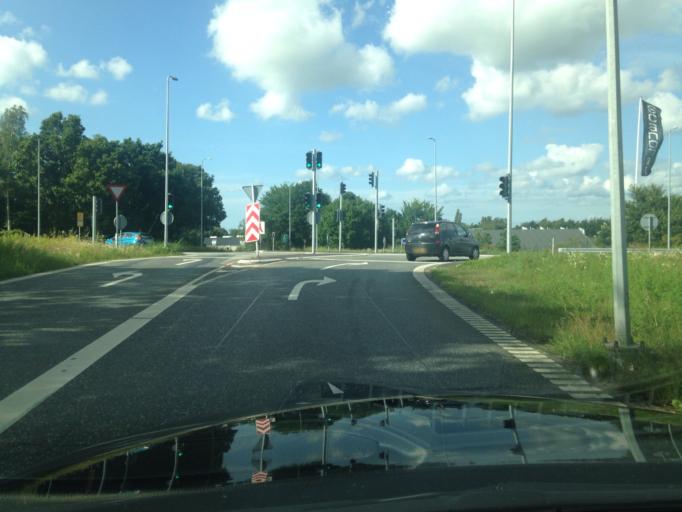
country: DK
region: Capital Region
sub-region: Fredensborg Kommune
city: Kokkedal
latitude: 55.9072
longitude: 12.4728
